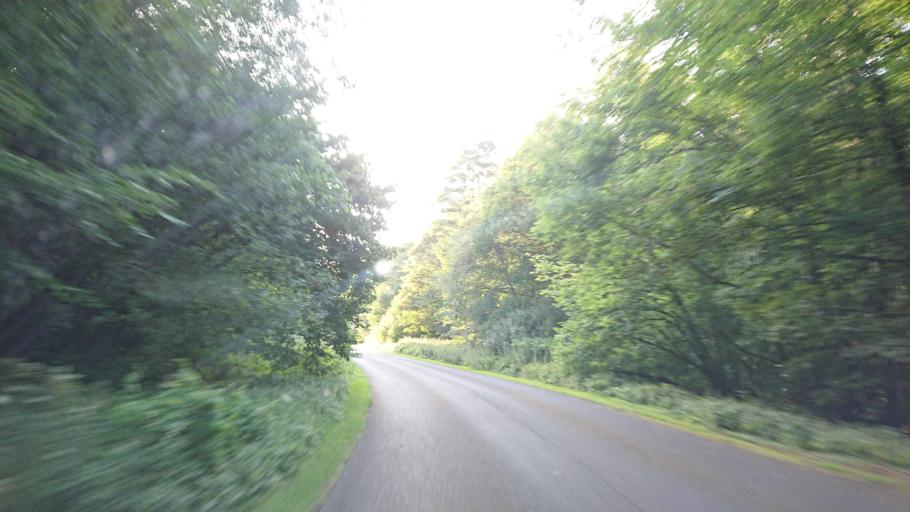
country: IE
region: Connaught
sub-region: Roscommon
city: Boyle
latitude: 53.9764
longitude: -8.2416
